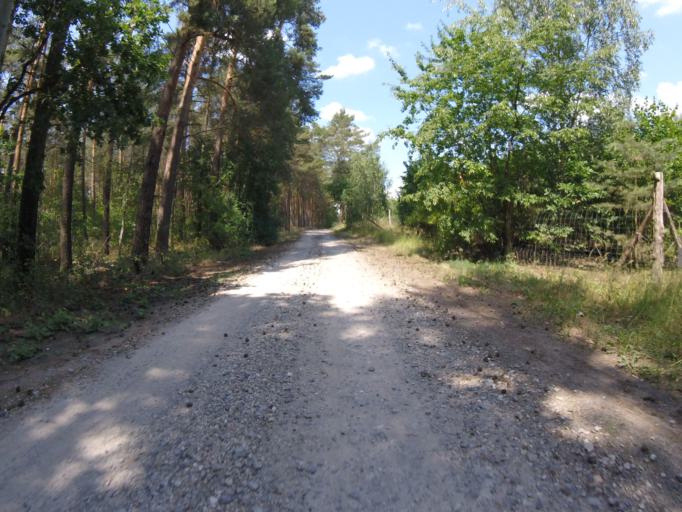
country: DE
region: Brandenburg
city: Bestensee
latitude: 52.2449
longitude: 13.6927
